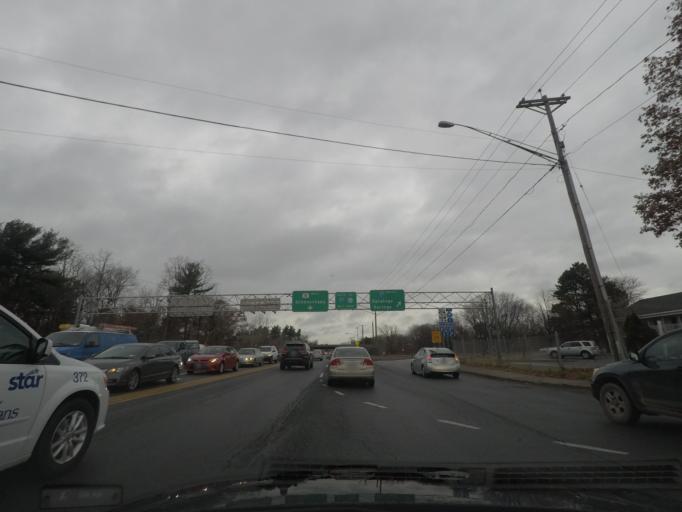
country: US
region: New York
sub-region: Albany County
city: Colonie
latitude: 42.7087
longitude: -73.8226
